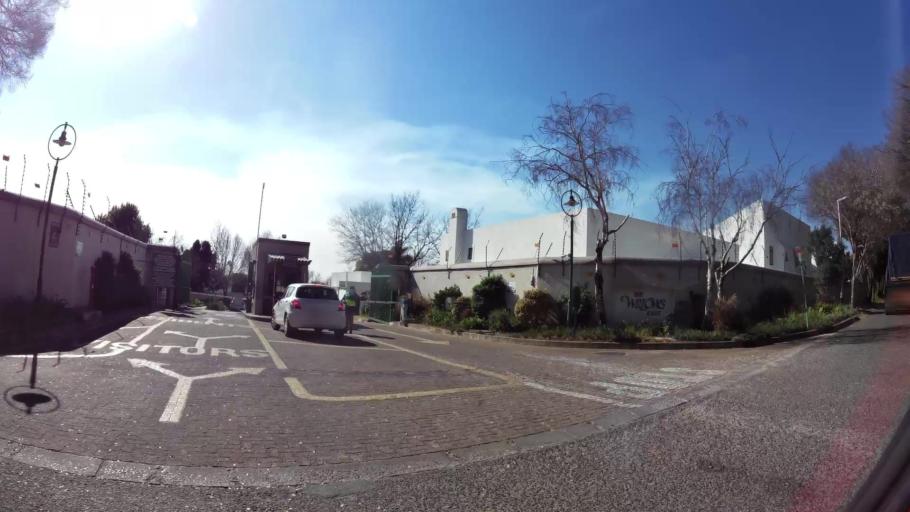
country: ZA
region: Gauteng
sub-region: City of Johannesburg Metropolitan Municipality
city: Roodepoort
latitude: -26.1192
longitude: 27.9629
